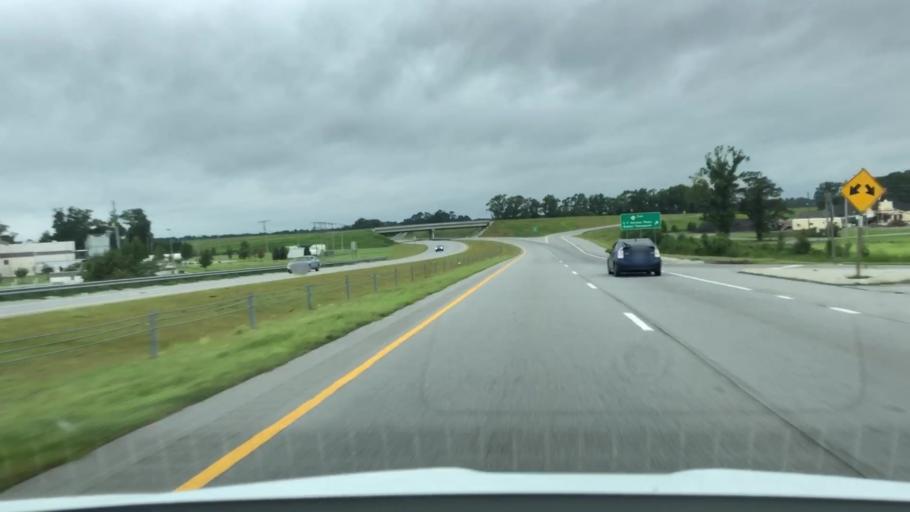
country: US
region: North Carolina
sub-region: Lenoir County
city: Kinston
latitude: 35.2635
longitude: -77.6691
